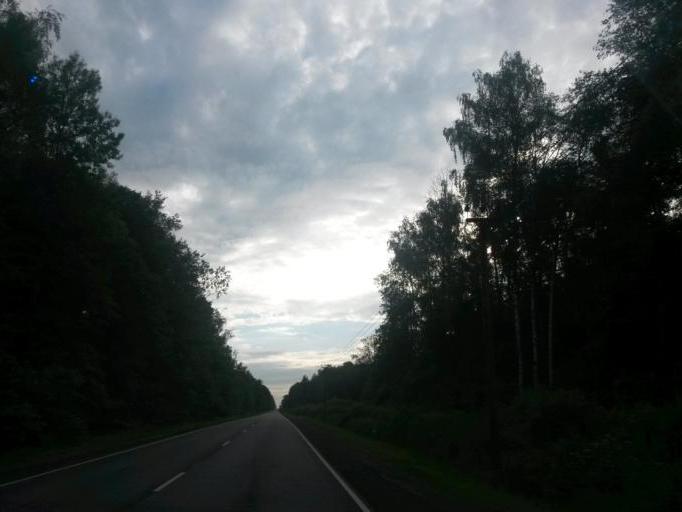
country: RU
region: Moskovskaya
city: Barybino
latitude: 55.1990
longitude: 37.8238
